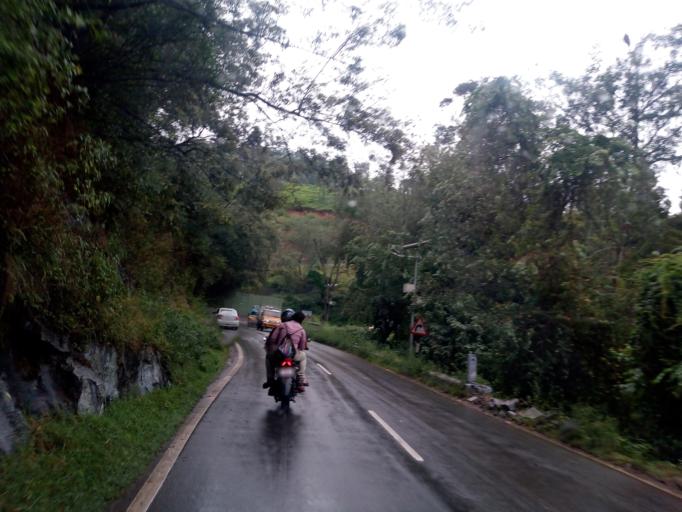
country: IN
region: Tamil Nadu
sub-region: Nilgiri
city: Wellington
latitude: 11.3589
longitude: 76.7827
